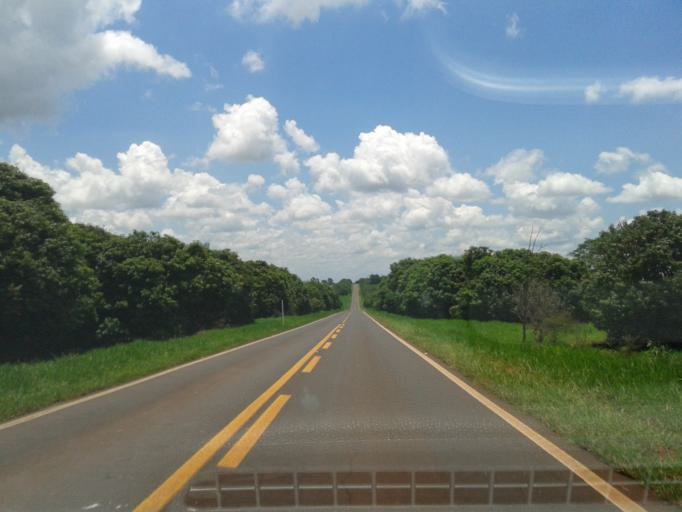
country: BR
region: Minas Gerais
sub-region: Centralina
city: Centralina
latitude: -18.7230
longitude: -49.1669
